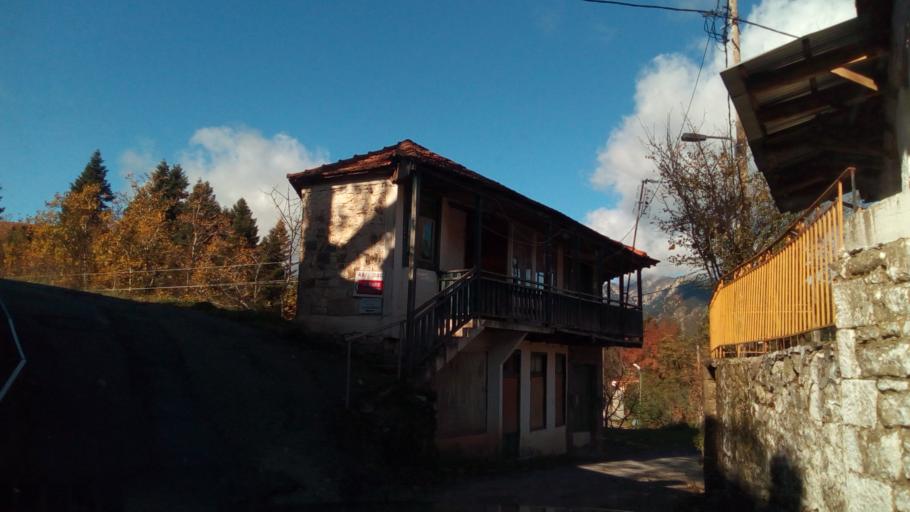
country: GR
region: West Greece
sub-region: Nomos Aitolias kai Akarnanias
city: Nafpaktos
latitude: 38.5928
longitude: 21.9235
